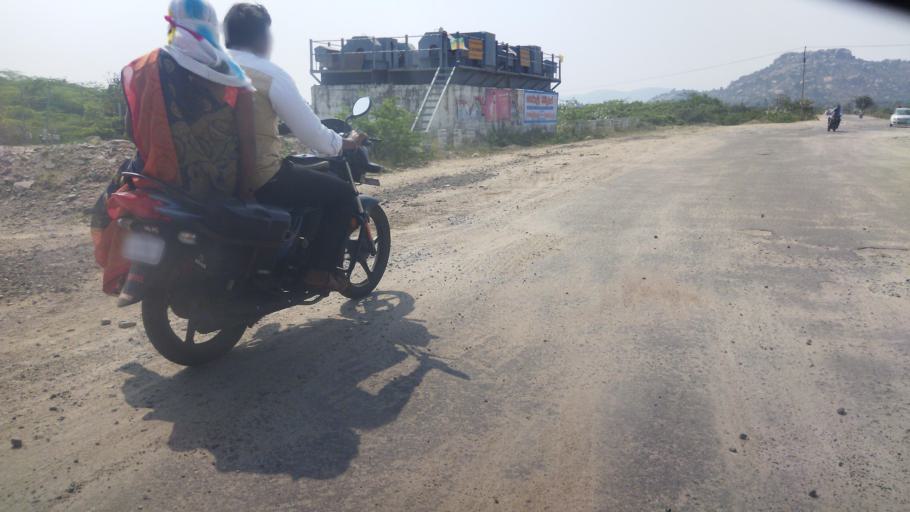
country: IN
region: Telangana
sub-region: Nalgonda
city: Nalgonda
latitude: 17.1140
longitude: 79.2813
